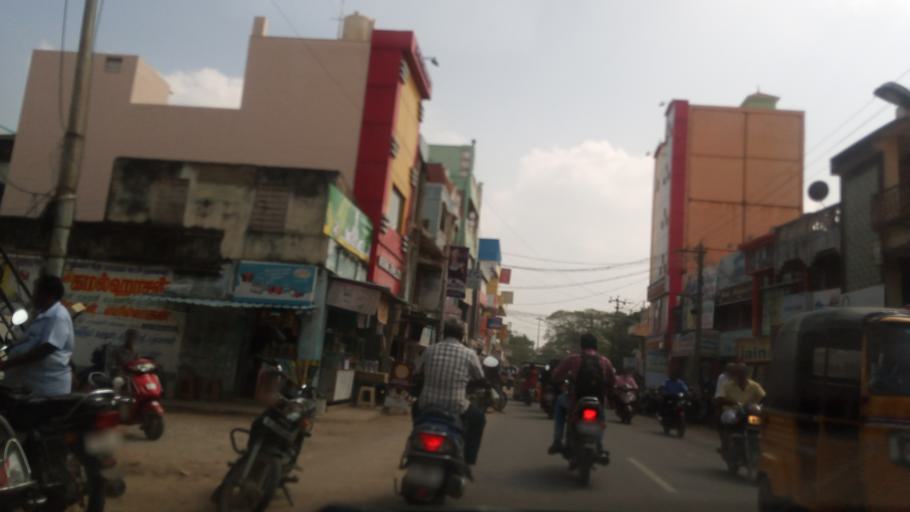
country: IN
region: Tamil Nadu
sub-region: Vellore
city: Arakkonam
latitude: 13.0857
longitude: 79.6639
